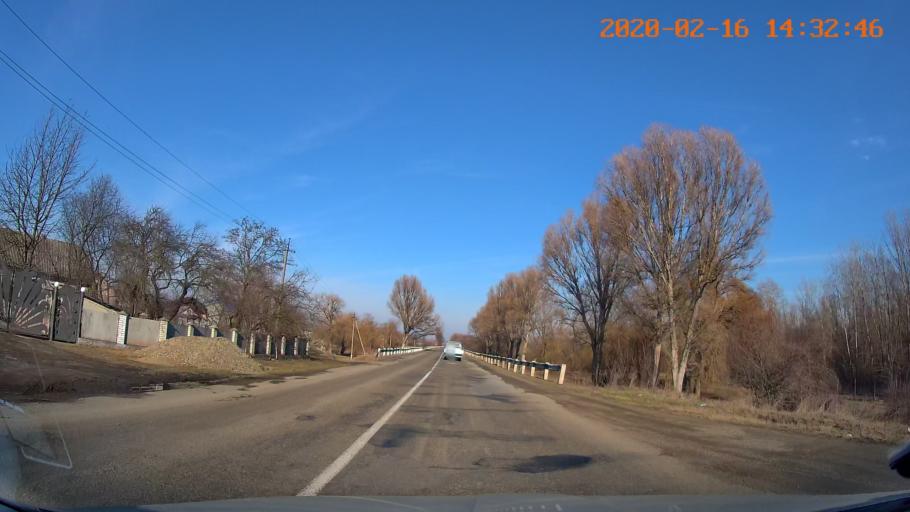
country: RO
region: Botosani
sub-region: Comuna Hudesti
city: Alba
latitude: 48.2154
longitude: 26.4573
